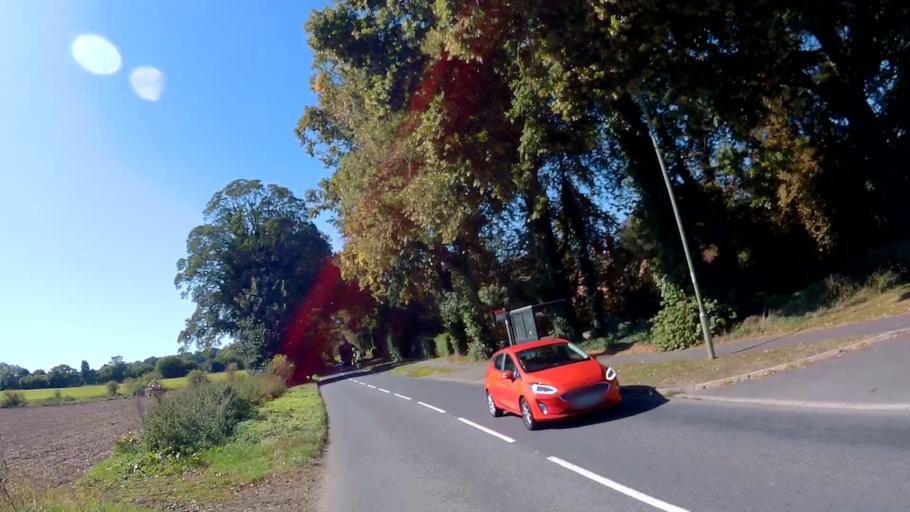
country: GB
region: England
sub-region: Hampshire
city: Overton
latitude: 51.2421
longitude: -1.2759
